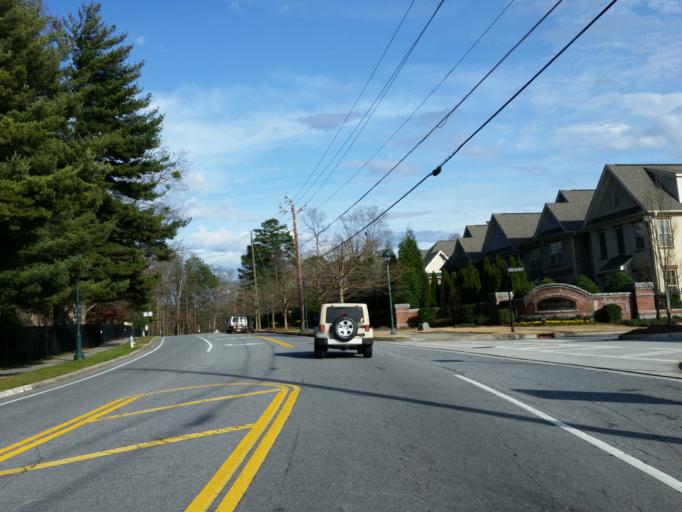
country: US
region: Georgia
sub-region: DeKalb County
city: Dunwoody
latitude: 33.9551
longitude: -84.3617
